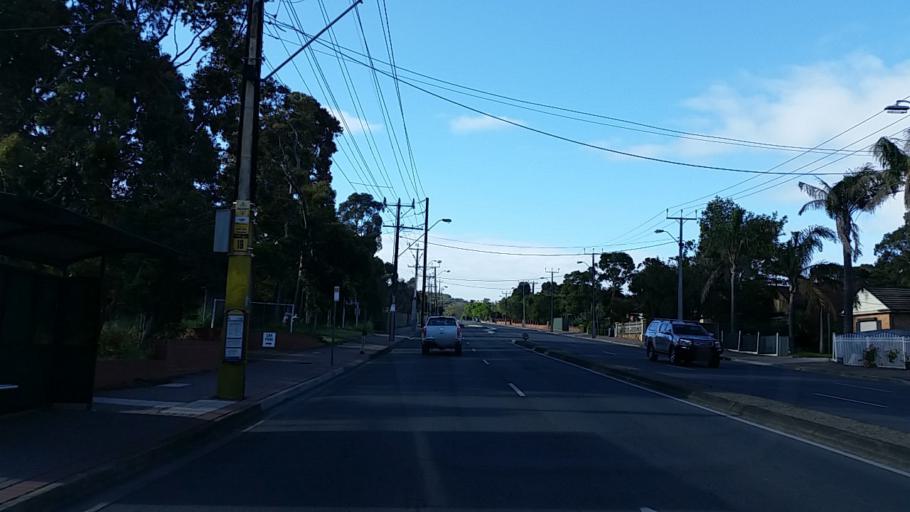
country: AU
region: South Australia
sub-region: Mitcham
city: Clapham
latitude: -34.9937
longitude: 138.5929
